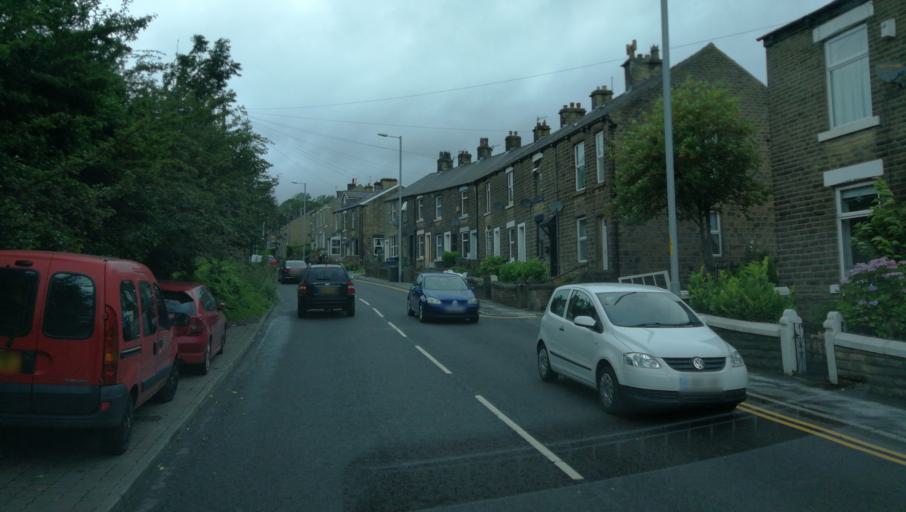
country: GB
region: England
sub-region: Borough of Tameside
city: Longdendale
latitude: 53.4598
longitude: -1.9940
